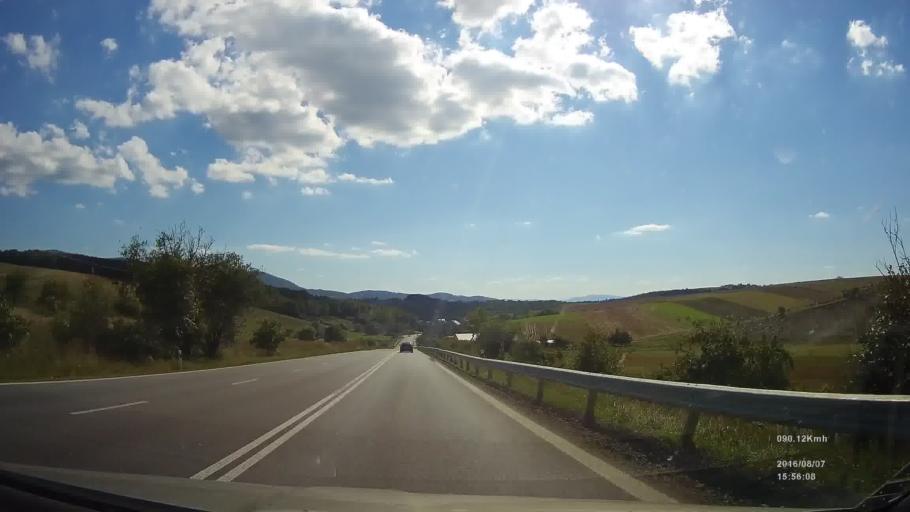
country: SK
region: Presovsky
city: Giraltovce
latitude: 49.0695
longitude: 21.4290
